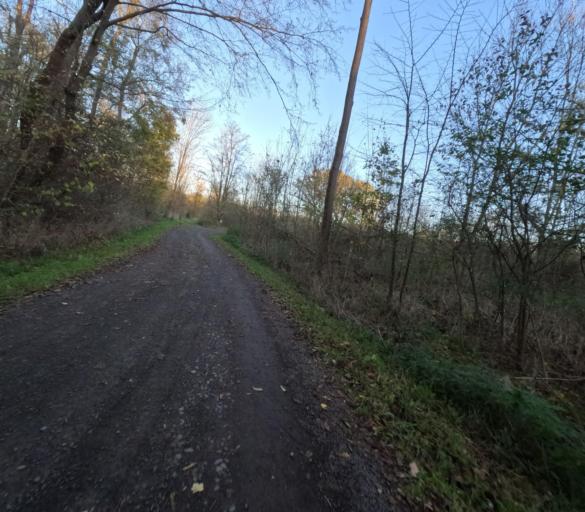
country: DE
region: Saxony
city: Schkeuditz
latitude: 51.3849
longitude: 12.1995
